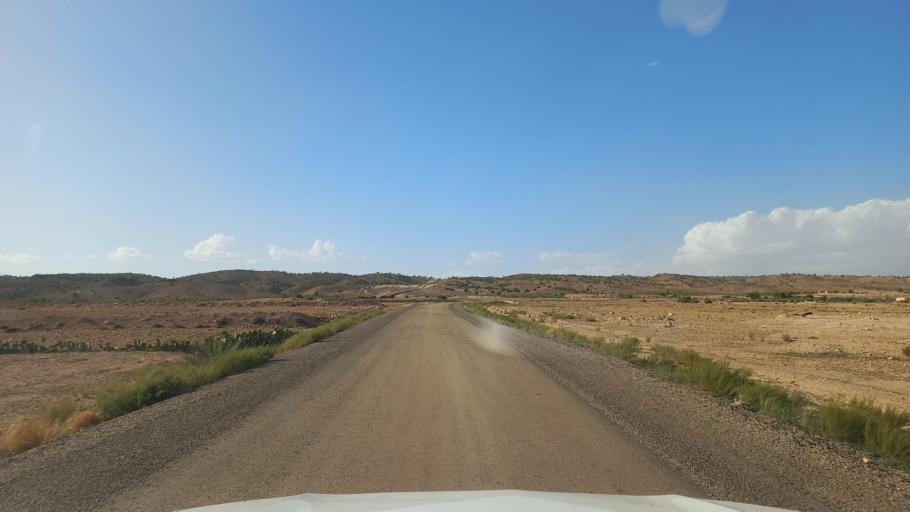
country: TN
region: Al Qasrayn
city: Sbiba
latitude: 35.3502
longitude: 8.9876
